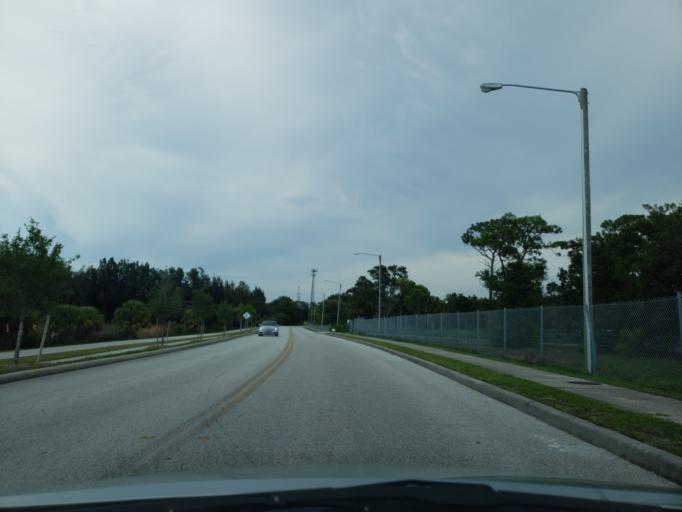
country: US
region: Florida
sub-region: Pinellas County
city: Tarpon Springs
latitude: 28.1539
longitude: -82.7522
